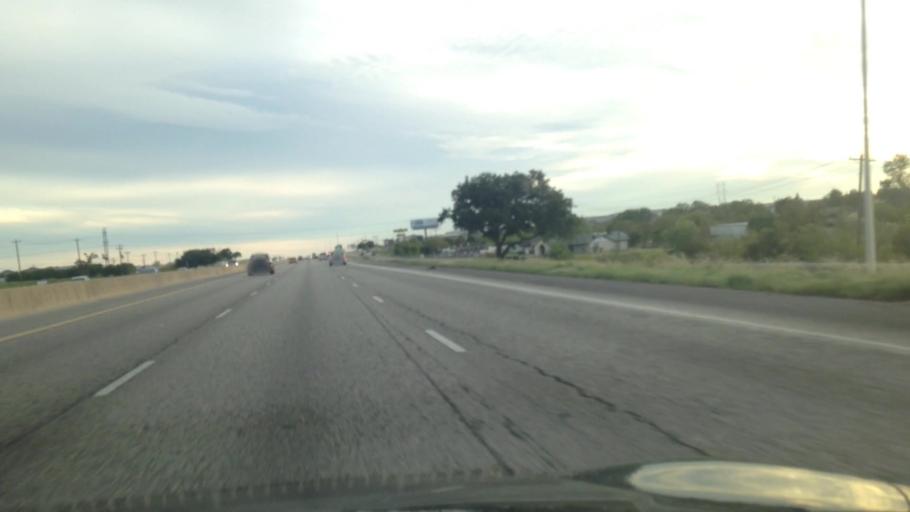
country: US
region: Texas
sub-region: Hays County
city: Buda
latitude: 30.0746
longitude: -97.8264
